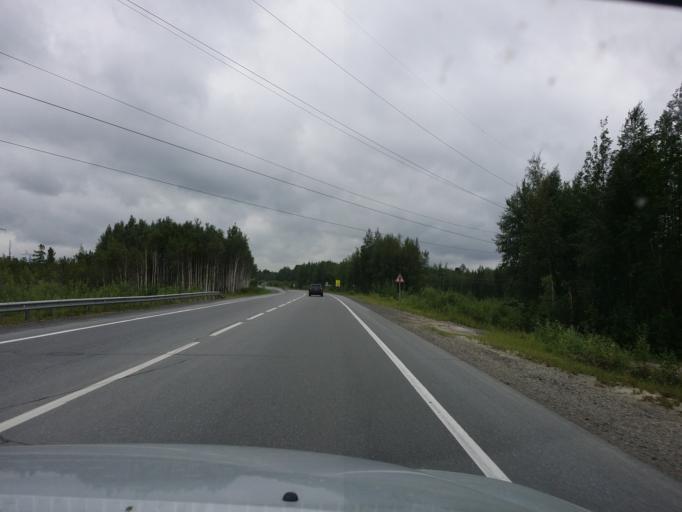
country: RU
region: Khanty-Mansiyskiy Avtonomnyy Okrug
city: Nizhnevartovsk
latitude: 61.0268
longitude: 76.3656
